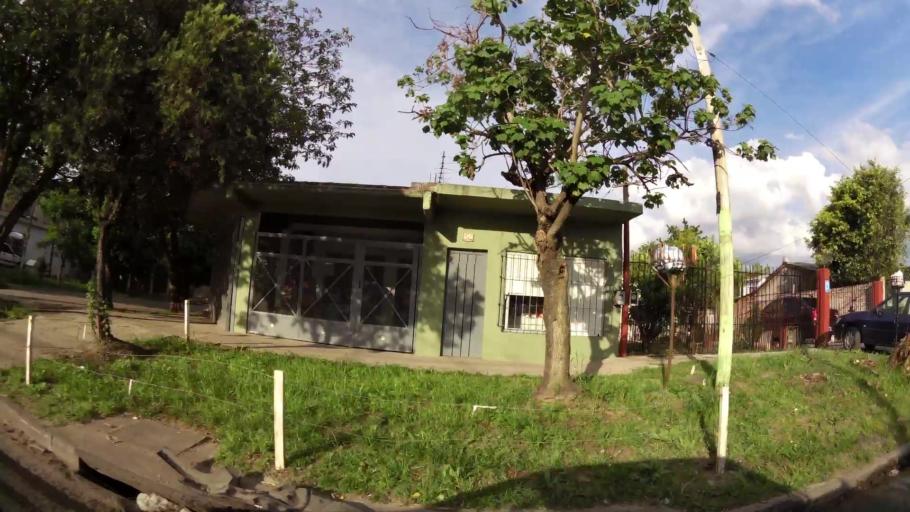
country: AR
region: Buenos Aires
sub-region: Partido de Quilmes
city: Quilmes
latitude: -34.7473
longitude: -58.2643
